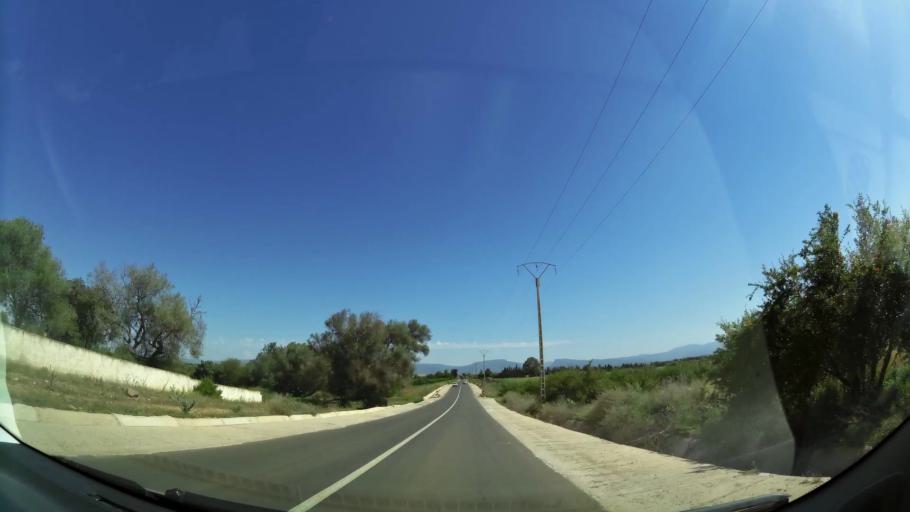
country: MA
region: Oriental
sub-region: Berkane-Taourirt
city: Madagh
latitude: 35.0233
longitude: -2.4096
